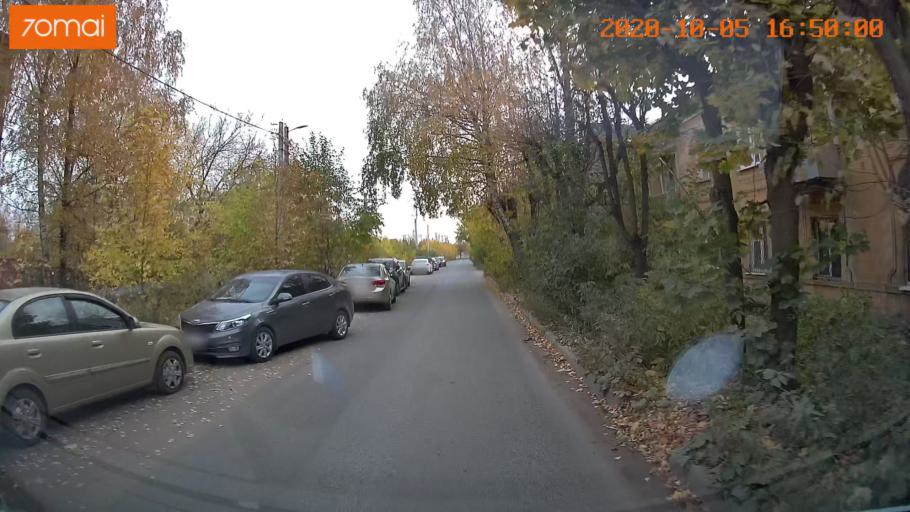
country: RU
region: Ivanovo
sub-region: Gorod Ivanovo
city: Ivanovo
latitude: 56.9656
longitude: 40.9778
